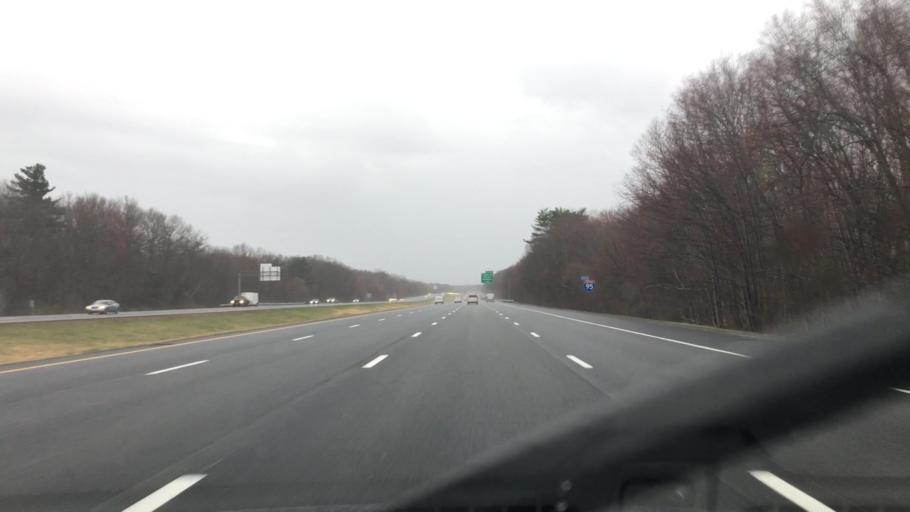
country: US
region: Massachusetts
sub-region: Essex County
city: West Newbury
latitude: 42.7736
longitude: -70.9309
